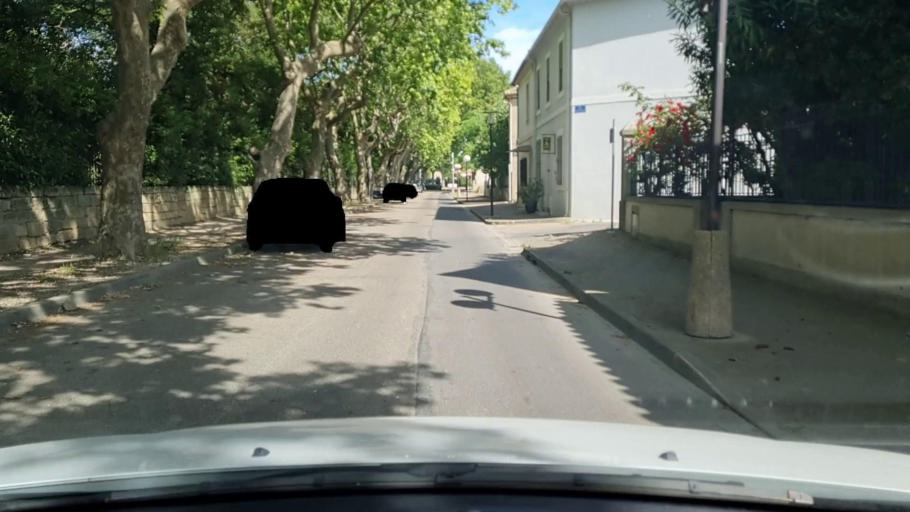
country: FR
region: Languedoc-Roussillon
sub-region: Departement de l'Herault
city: Marsillargues
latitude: 43.6363
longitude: 4.1957
